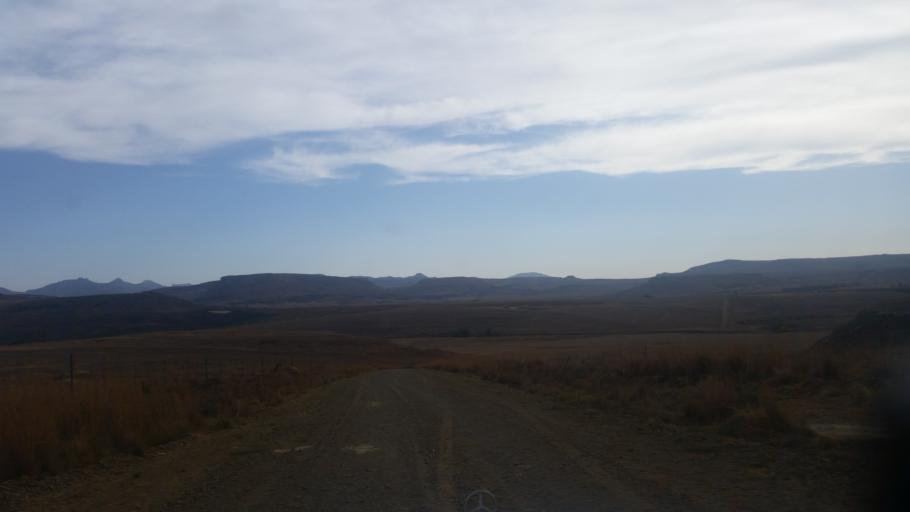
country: ZA
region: Orange Free State
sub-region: Thabo Mofutsanyana District Municipality
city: Phuthaditjhaba
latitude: -28.4012
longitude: 28.7683
